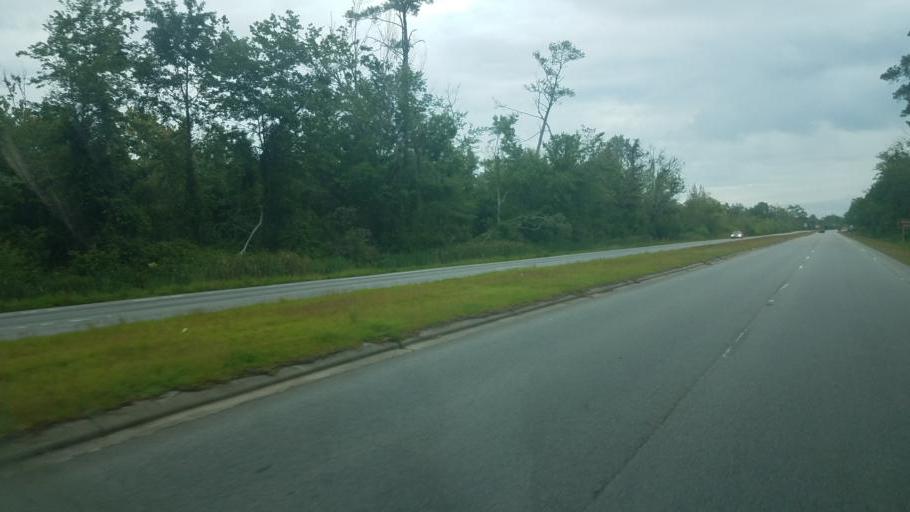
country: US
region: North Carolina
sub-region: Tyrrell County
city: Columbia
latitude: 35.9152
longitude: -76.2674
